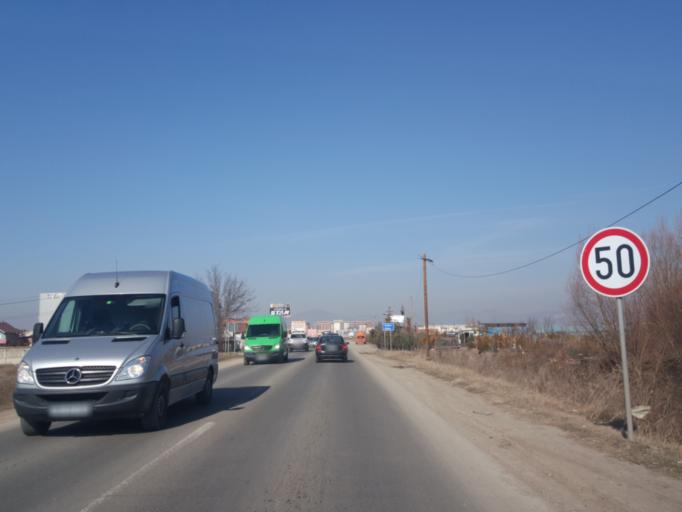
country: XK
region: Mitrovica
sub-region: Vushtrri
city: Vushtrri
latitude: 42.8099
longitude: 20.9873
